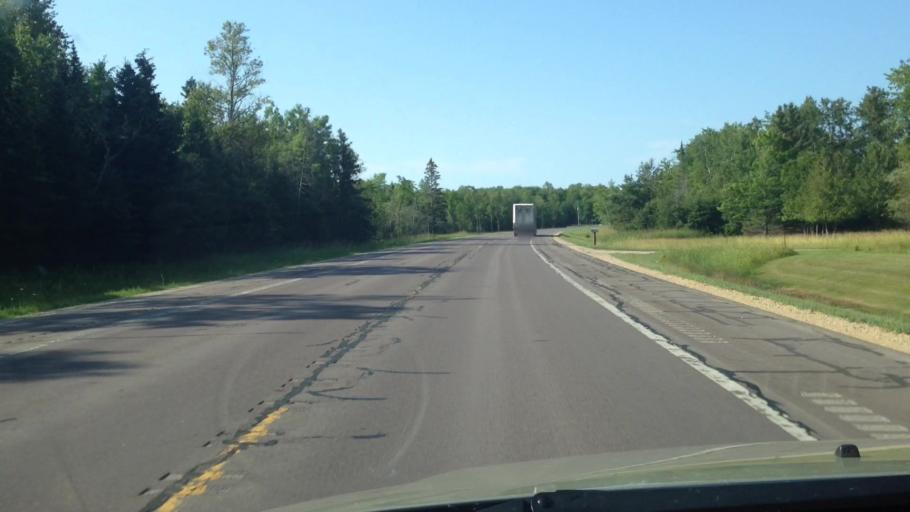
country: US
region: Michigan
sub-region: Schoolcraft County
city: Manistique
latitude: 46.0610
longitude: -85.9588
